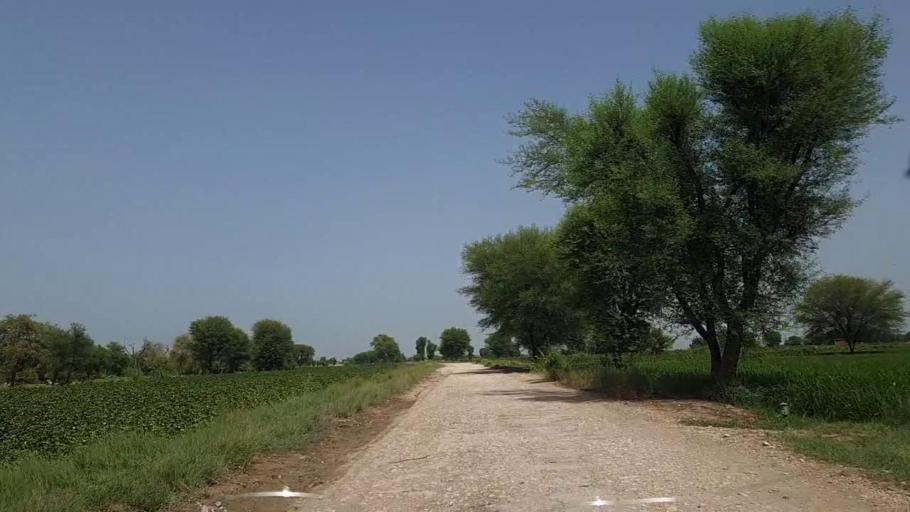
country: PK
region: Sindh
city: Tharu Shah
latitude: 27.0138
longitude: 68.1380
